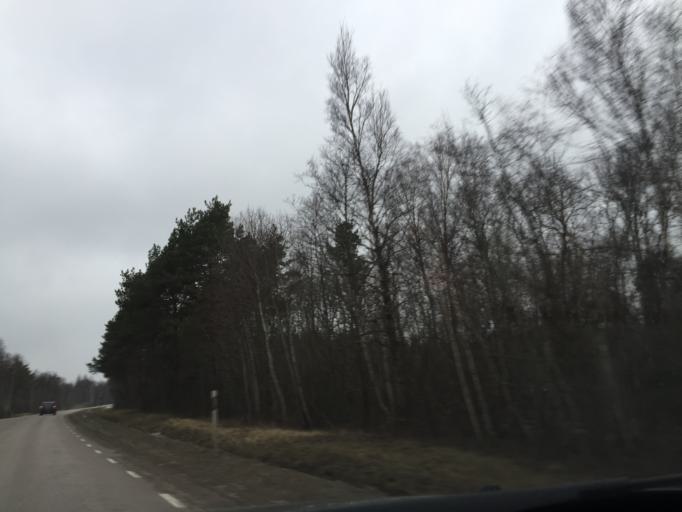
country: EE
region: Saare
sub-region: Kuressaare linn
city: Kuressaare
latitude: 58.2887
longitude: 22.3934
